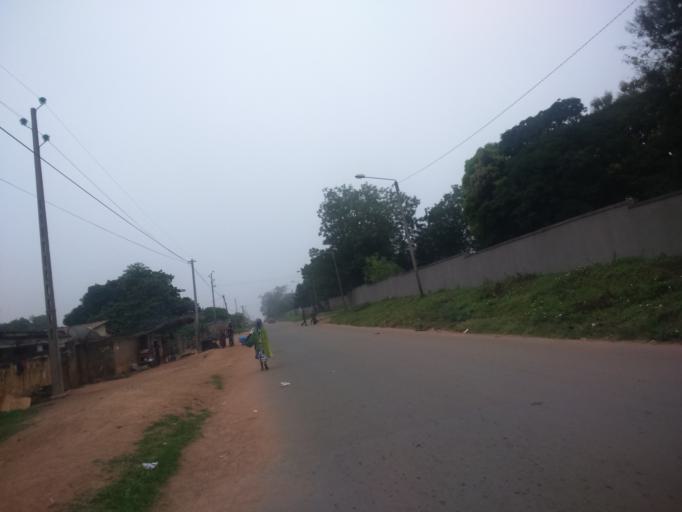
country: CI
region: Zanzan
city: Bondoukou
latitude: 8.0456
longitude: -2.7895
